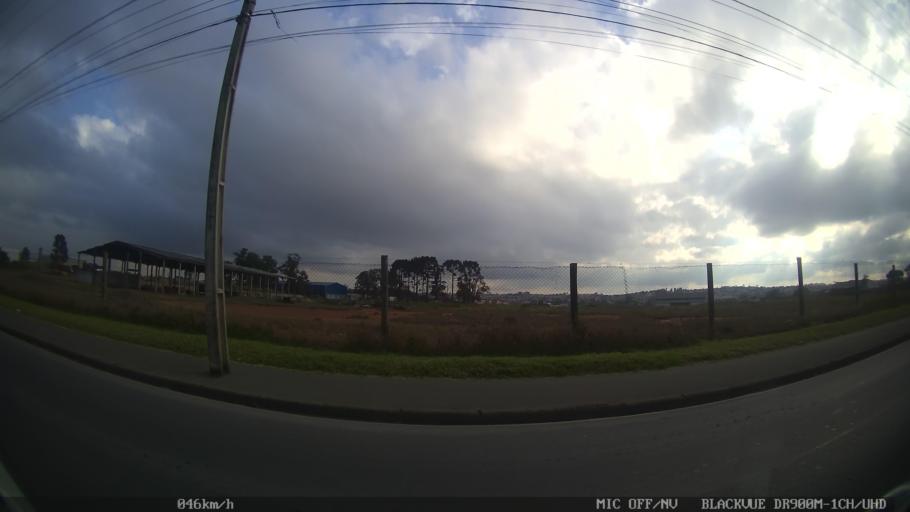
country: BR
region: Parana
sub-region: Pinhais
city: Pinhais
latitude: -25.4087
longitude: -49.1823
